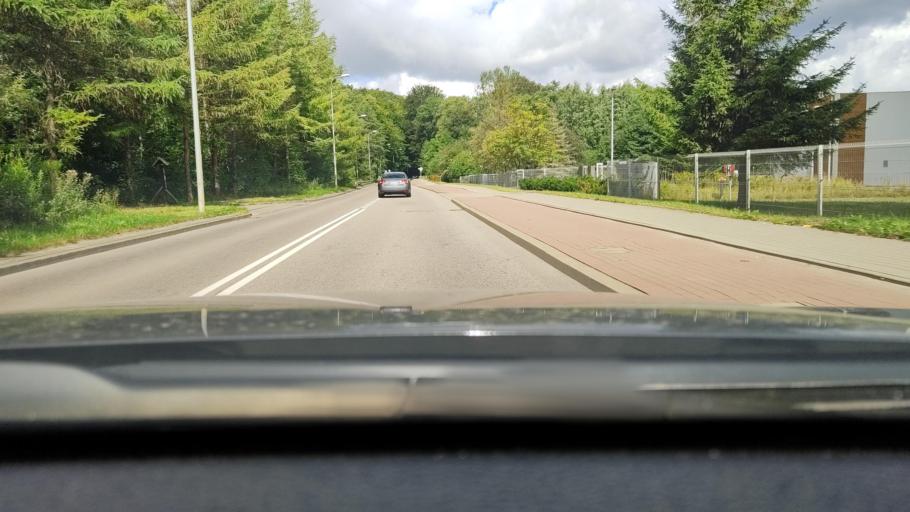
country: PL
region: Pomeranian Voivodeship
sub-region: Powiat wejherowski
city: Wejherowo
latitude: 54.5913
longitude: 18.2403
